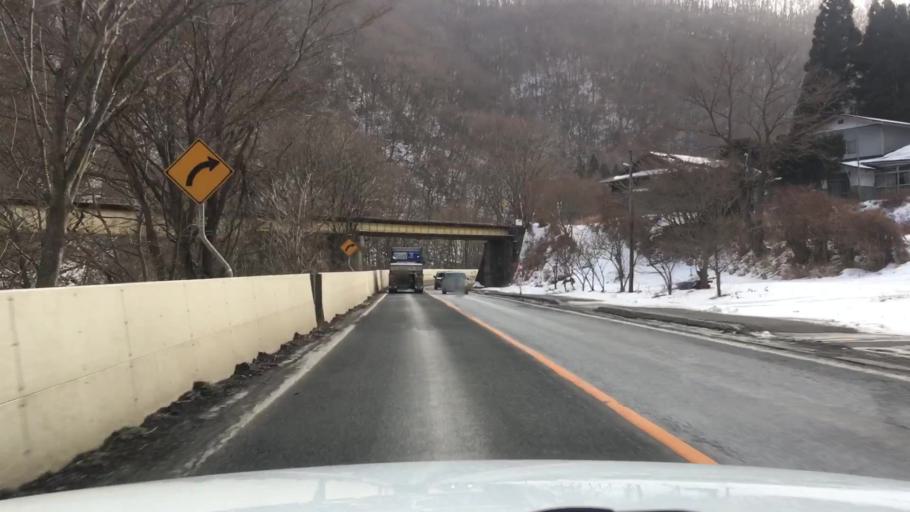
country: JP
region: Iwate
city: Tono
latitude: 39.6254
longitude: 141.5138
